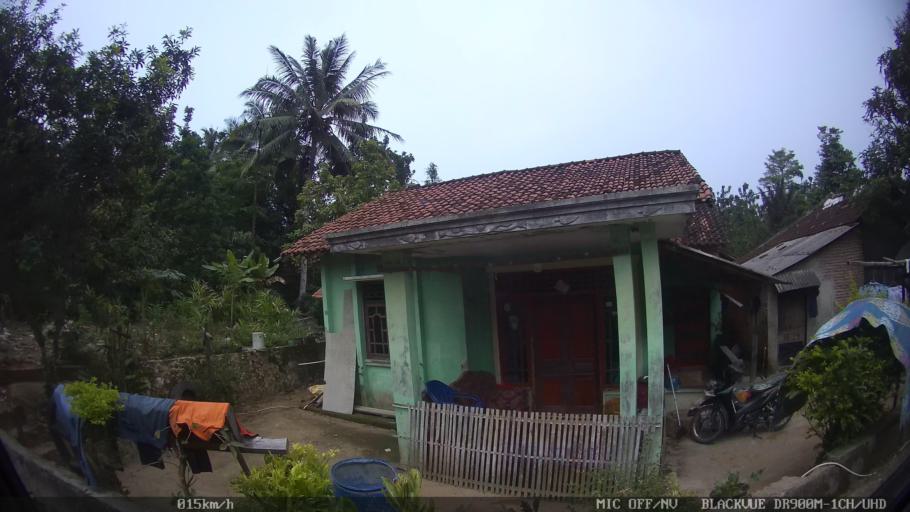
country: ID
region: Lampung
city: Bandarlampung
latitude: -5.4262
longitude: 105.3087
